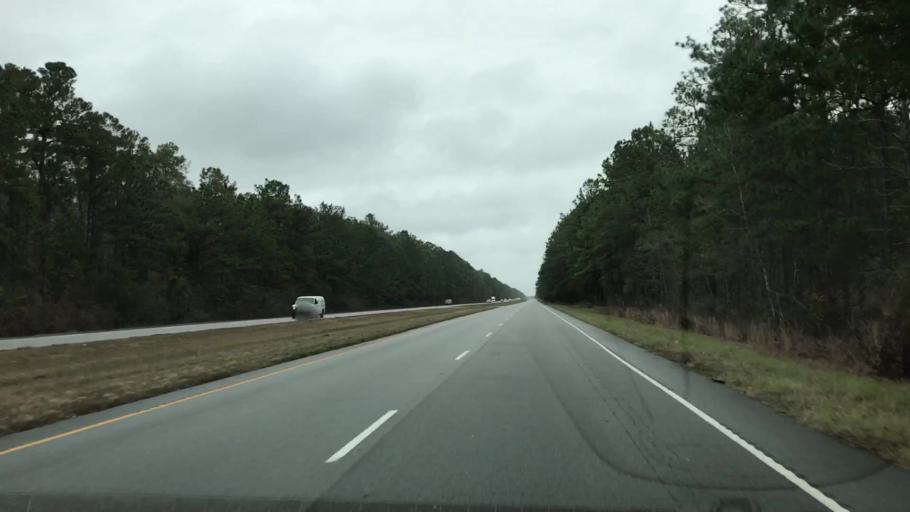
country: US
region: South Carolina
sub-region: Charleston County
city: Awendaw
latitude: 33.1437
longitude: -79.4376
